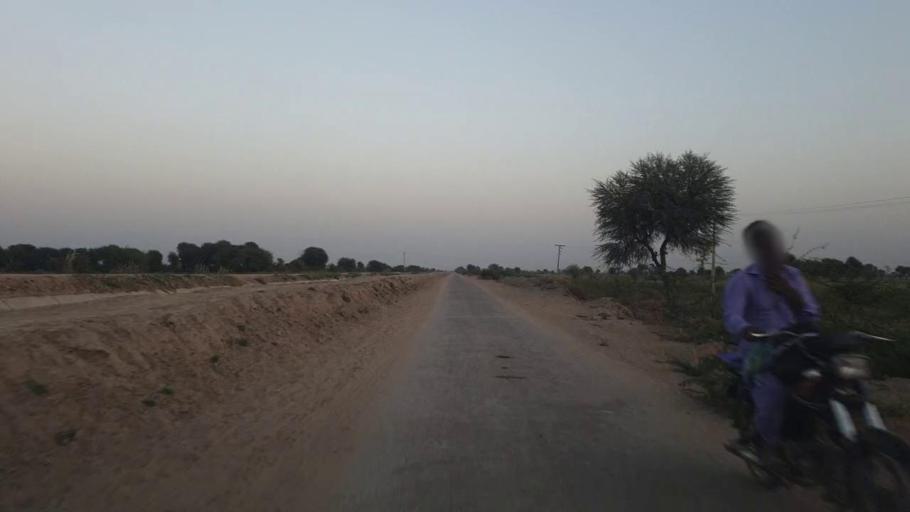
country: PK
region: Sindh
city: Umarkot
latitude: 25.4179
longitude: 69.6706
